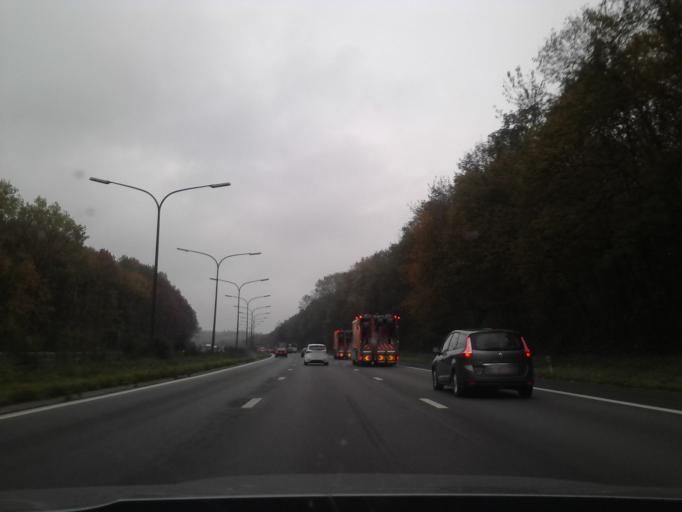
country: BE
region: Wallonia
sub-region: Province du Brabant Wallon
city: Braine-le-Chateau
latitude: 50.7134
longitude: 4.2662
